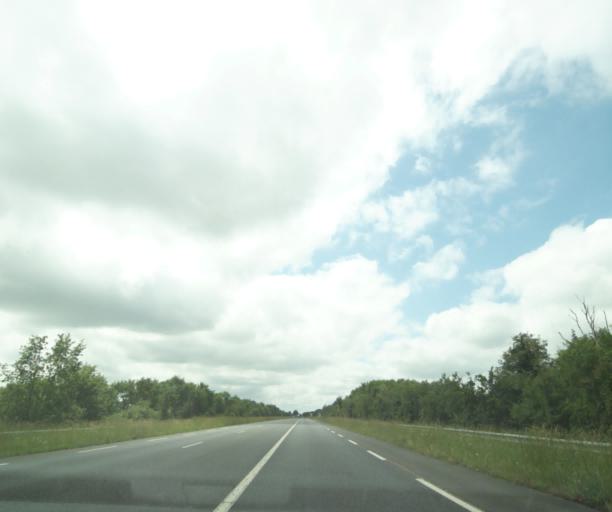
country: FR
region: Poitou-Charentes
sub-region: Departement des Deux-Sevres
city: Airvault
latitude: 46.7828
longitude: -0.2171
